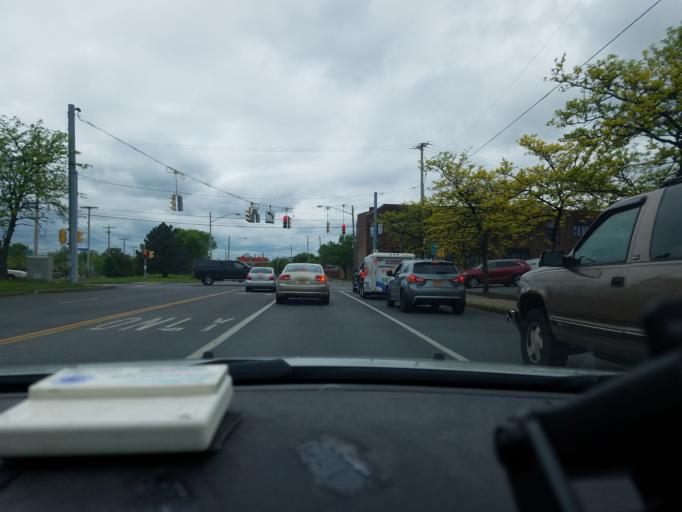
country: US
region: New York
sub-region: Onondaga County
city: Syracuse
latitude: 43.0504
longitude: -76.1271
